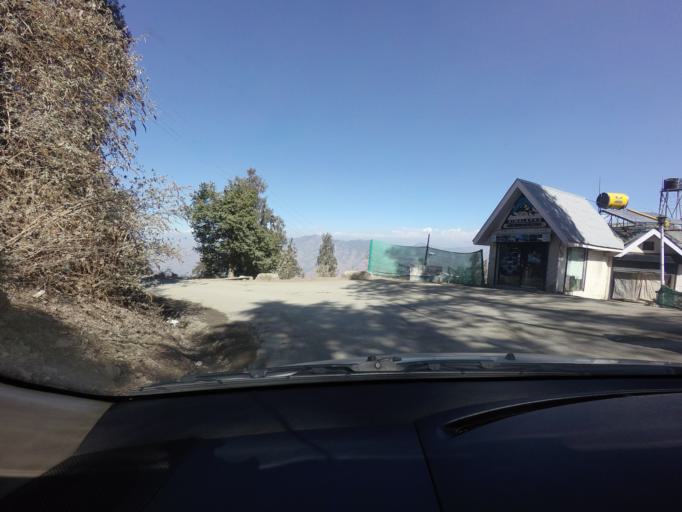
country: IN
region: Himachal Pradesh
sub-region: Shimla
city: Theog
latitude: 31.0989
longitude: 77.2674
